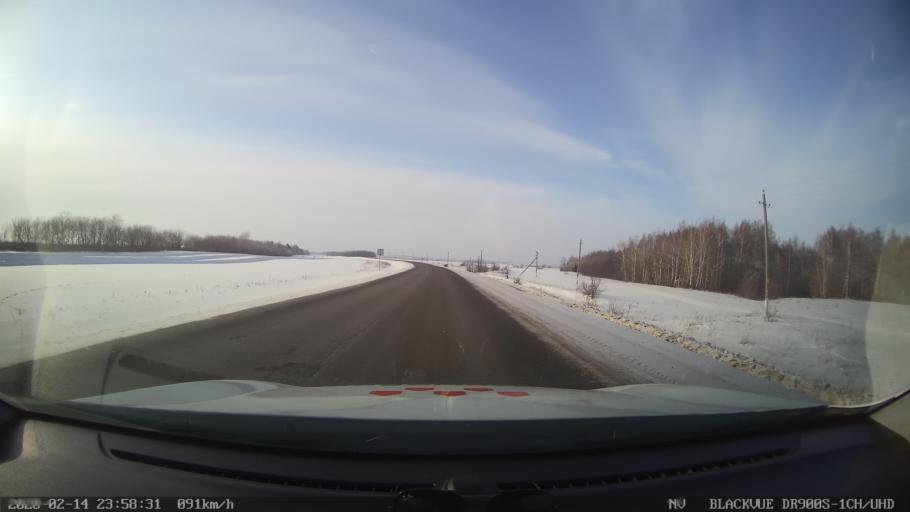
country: RU
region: Tatarstan
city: Kuybyshevskiy Zaton
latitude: 55.3412
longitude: 49.0854
